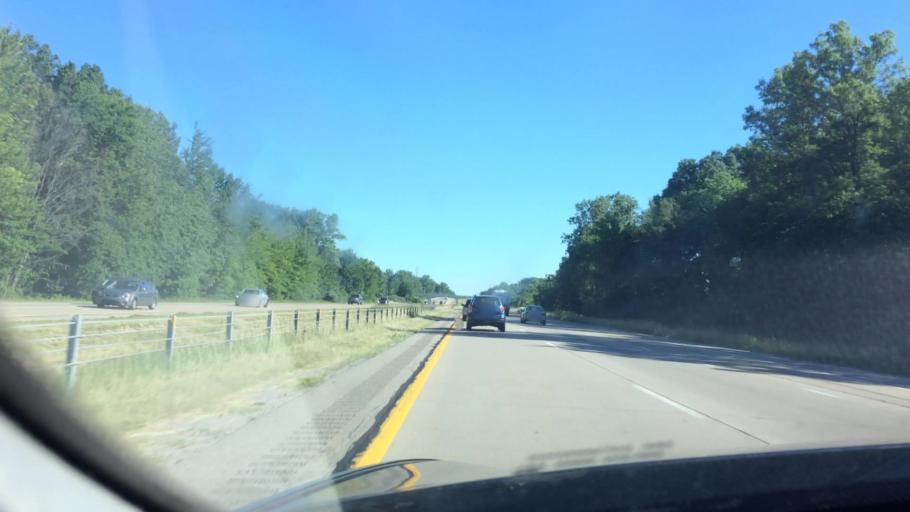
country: US
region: Michigan
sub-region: Monroe County
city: Dundee
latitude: 41.9048
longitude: -83.6617
